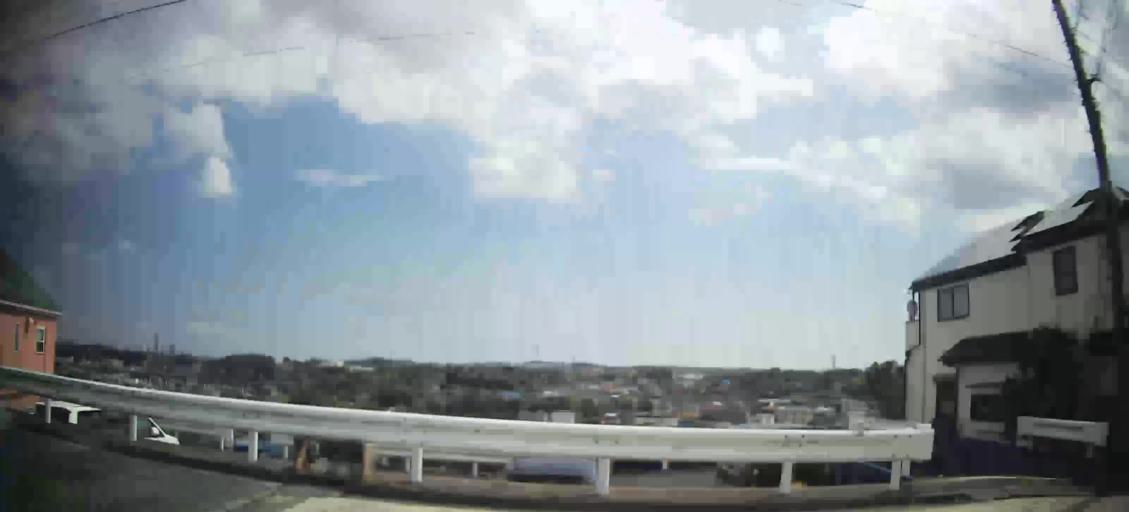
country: JP
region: Kanagawa
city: Yokohama
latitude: 35.4801
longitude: 139.5555
